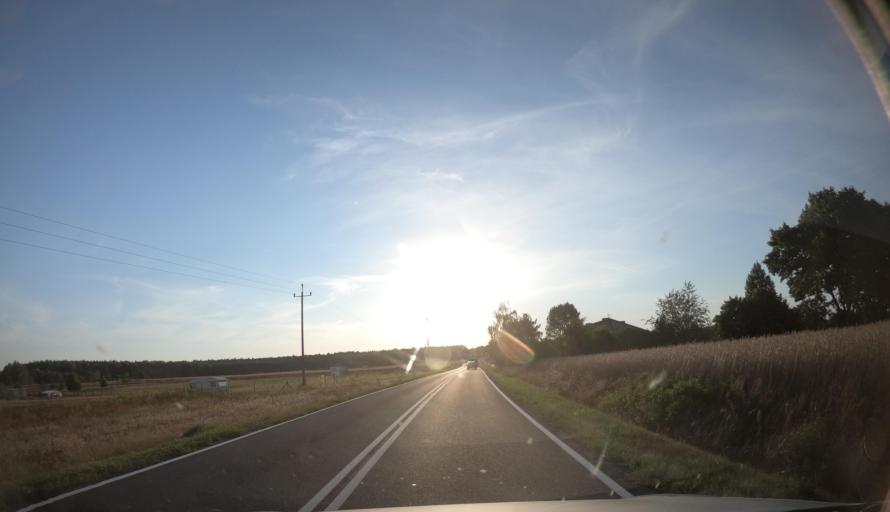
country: PL
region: Kujawsko-Pomorskie
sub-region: Powiat swiecki
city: Swiekatowo
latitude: 53.3047
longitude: 18.0706
